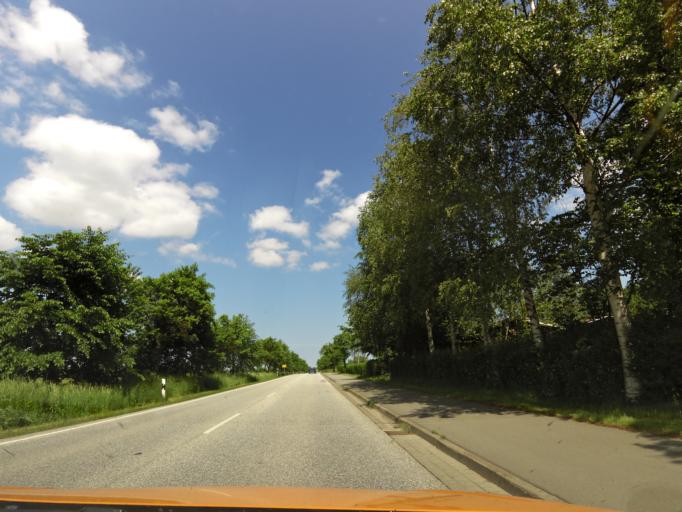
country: DE
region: Mecklenburg-Vorpommern
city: Rehna
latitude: 53.7590
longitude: 11.0511
